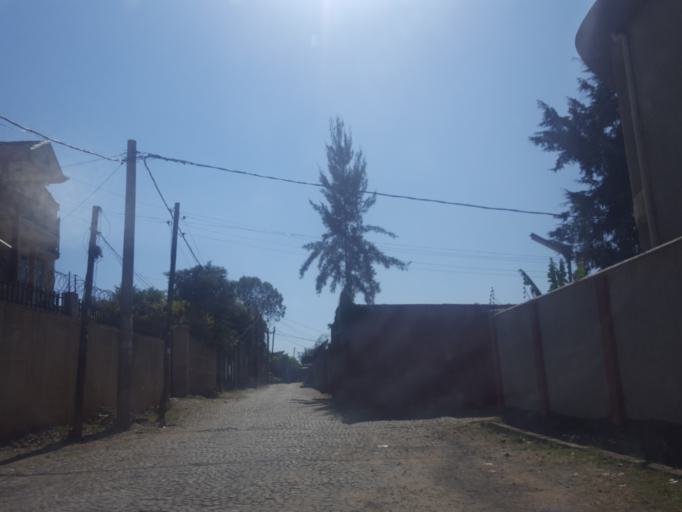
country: ET
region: Adis Abeba
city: Addis Ababa
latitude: 9.0549
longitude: 38.7241
